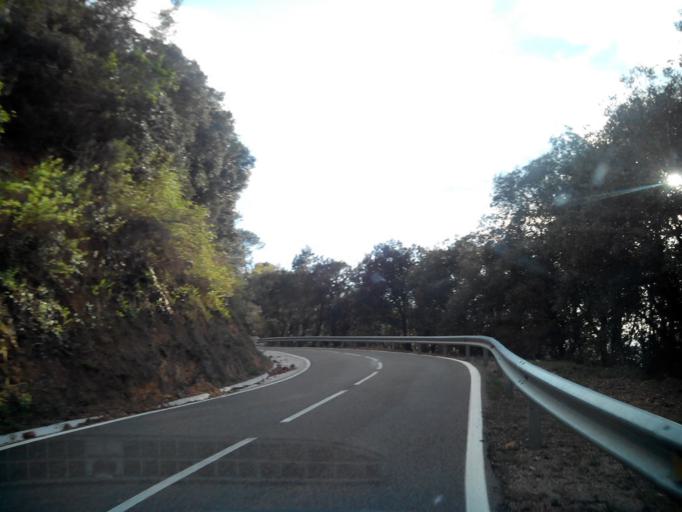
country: ES
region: Catalonia
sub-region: Provincia de Tarragona
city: Vilaplana
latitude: 41.2367
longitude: 1.0522
